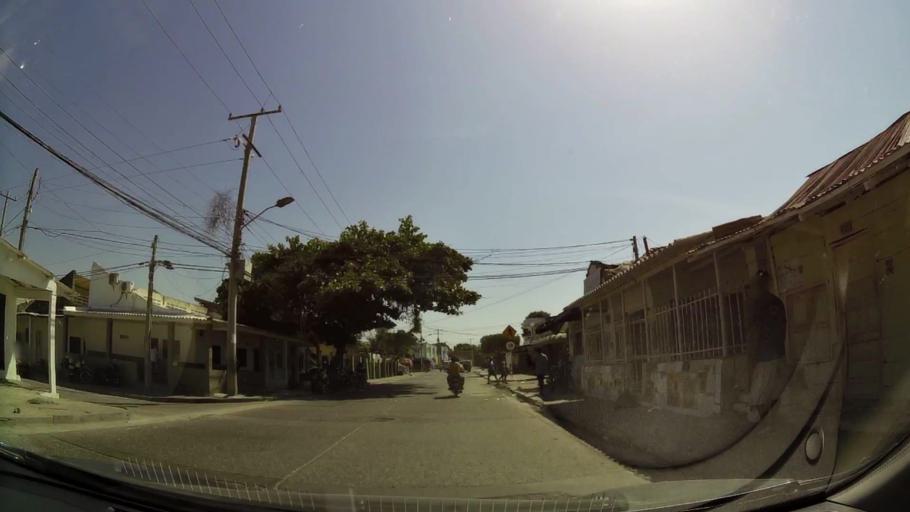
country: CO
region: Bolivar
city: Cartagena
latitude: 10.4172
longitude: -75.5197
